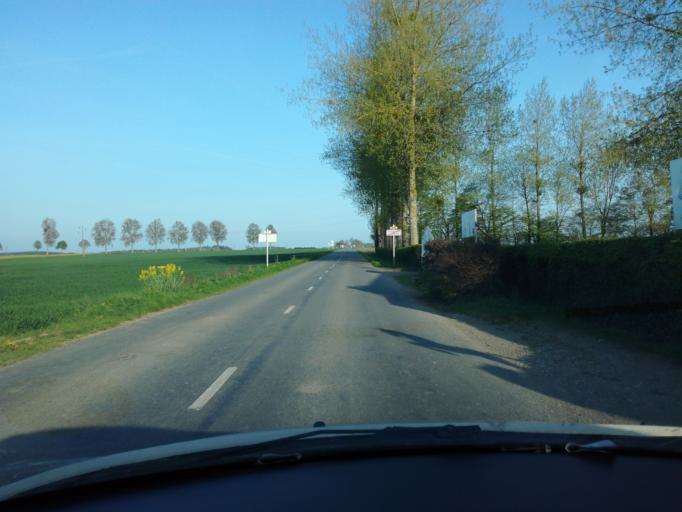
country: FR
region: Picardie
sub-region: Departement de la Somme
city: Poix-de-Picardie
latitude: 49.8241
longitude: 1.9479
